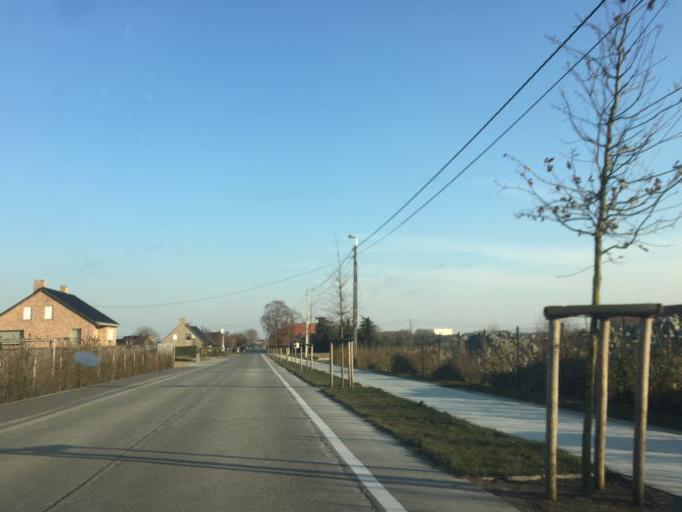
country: BE
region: Flanders
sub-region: Provincie West-Vlaanderen
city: Oostrozebeke
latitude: 50.9296
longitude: 3.3120
